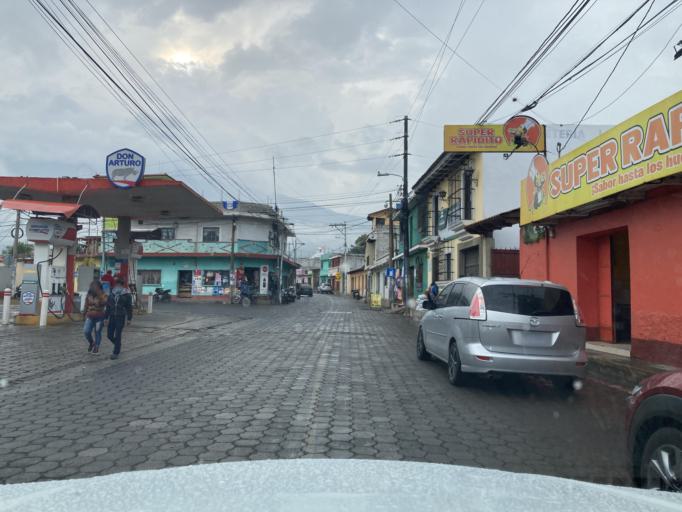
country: GT
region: Sacatepequez
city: San Miguel Duenas
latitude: 14.5246
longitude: -90.7972
